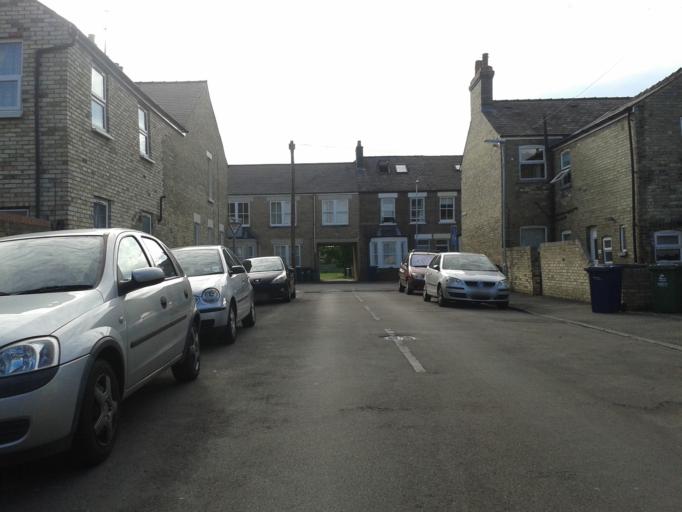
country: GB
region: England
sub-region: Cambridgeshire
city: Cambridge
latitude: 52.2003
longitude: 0.1446
